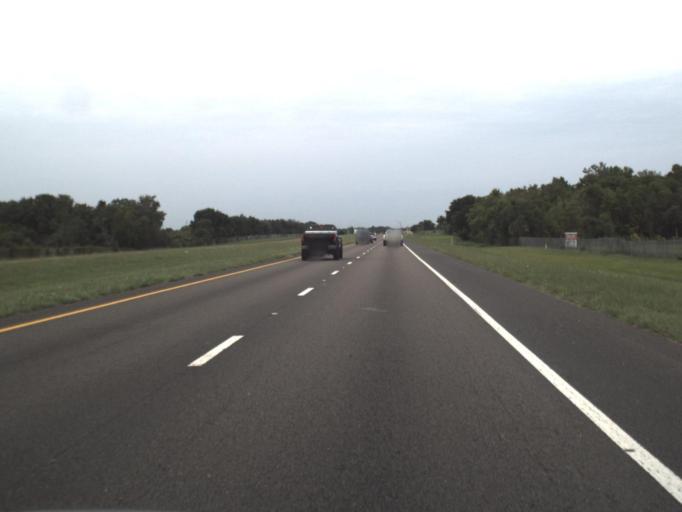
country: US
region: Florida
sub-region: Manatee County
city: Whitfield
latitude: 27.4072
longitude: -82.5328
